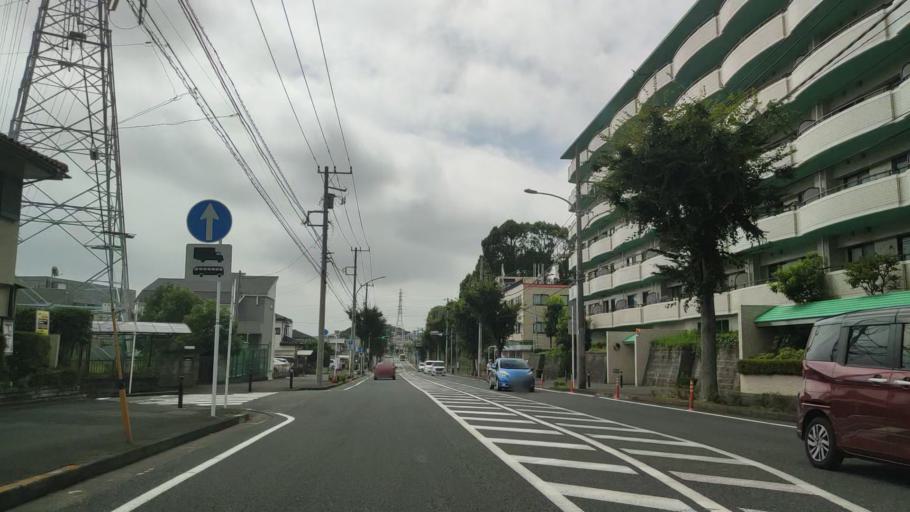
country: JP
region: Kanagawa
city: Fujisawa
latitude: 35.4150
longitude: 139.5224
